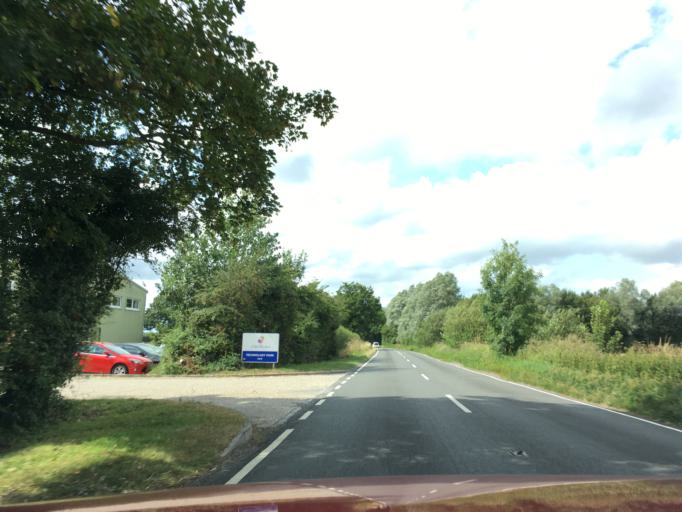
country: GB
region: England
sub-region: Kent
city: Tenterden
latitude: 51.0631
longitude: 0.7147
